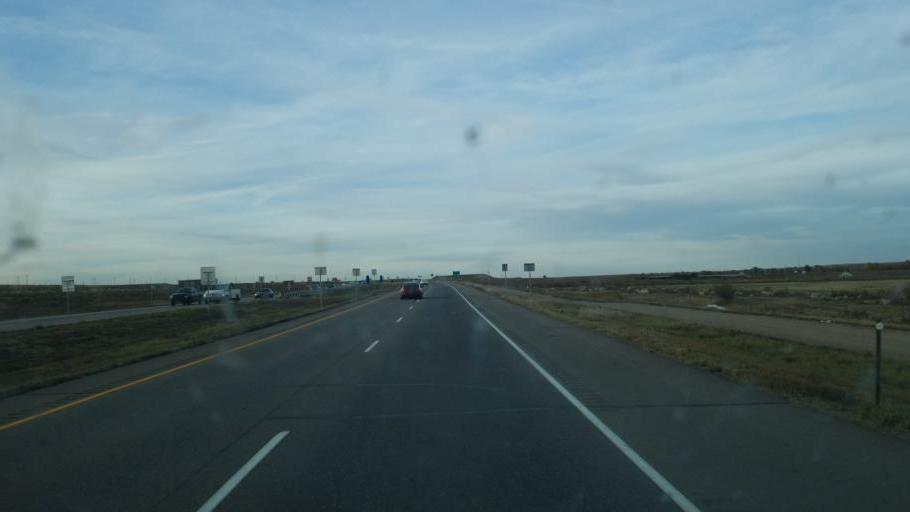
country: US
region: Colorado
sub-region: Pueblo County
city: Pueblo West
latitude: 38.3801
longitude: -104.6191
